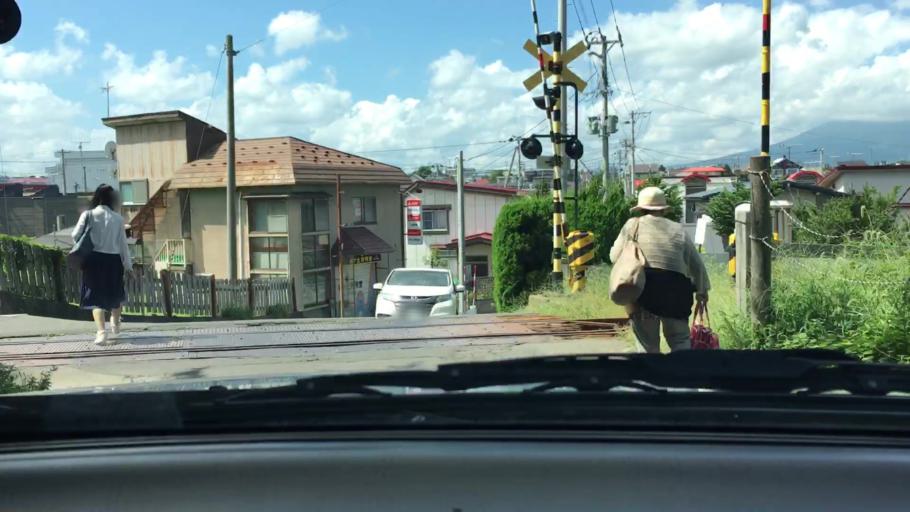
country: JP
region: Aomori
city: Hirosaki
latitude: 40.5882
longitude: 140.4694
